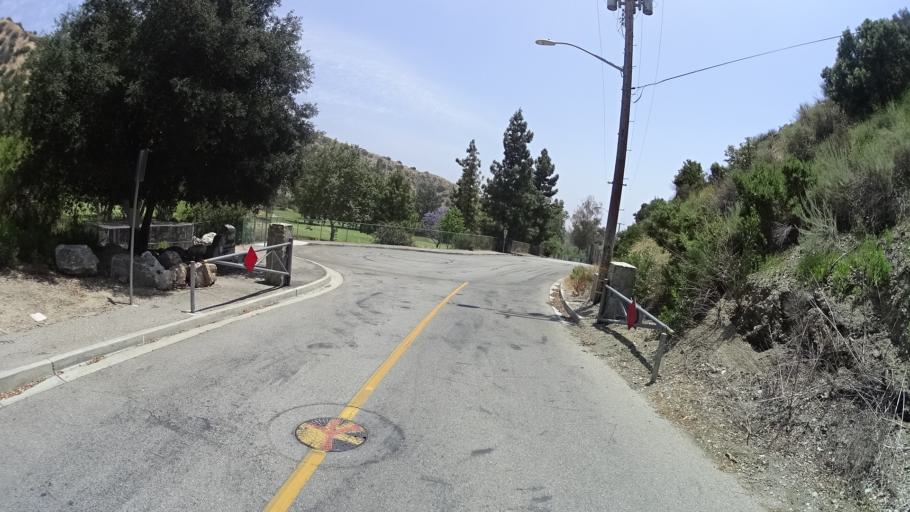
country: US
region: California
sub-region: Los Angeles County
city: Burbank
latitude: 34.2120
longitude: -118.3054
